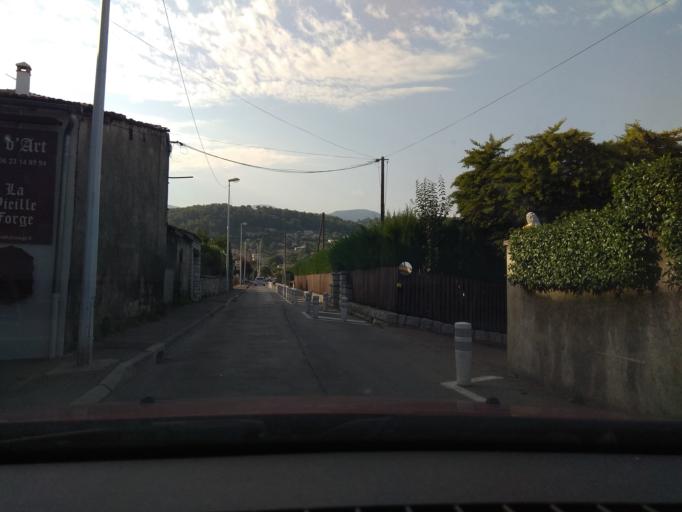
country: FR
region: Provence-Alpes-Cote d'Azur
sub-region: Departement des Alpes-Maritimes
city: La Colle-sur-Loup
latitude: 43.6857
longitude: 7.1078
